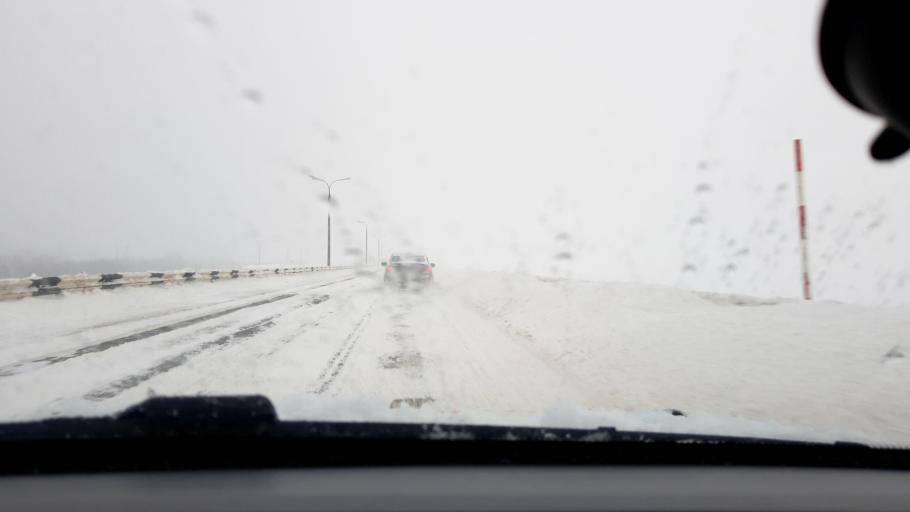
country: RU
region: Nizjnij Novgorod
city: Pervomayskiy
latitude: 56.6444
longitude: 43.3337
